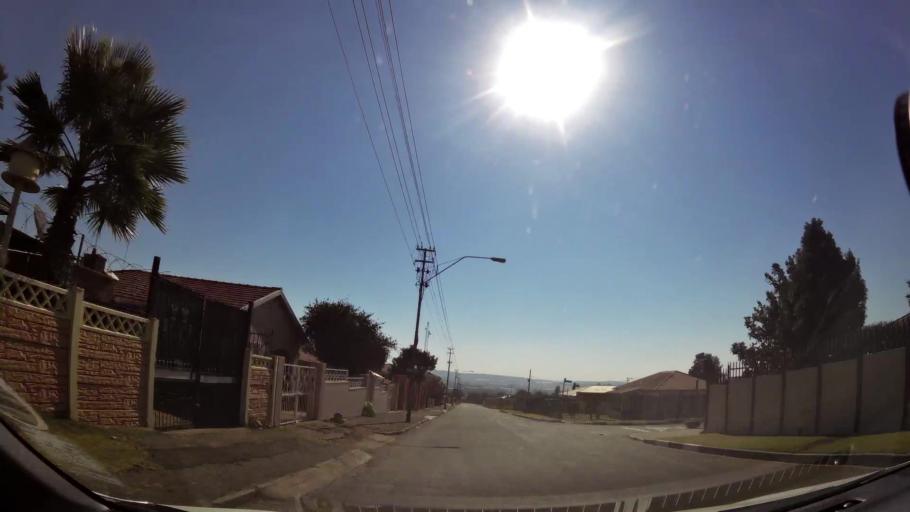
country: ZA
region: Gauteng
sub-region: City of Johannesburg Metropolitan Municipality
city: Johannesburg
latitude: -26.2475
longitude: 28.0852
